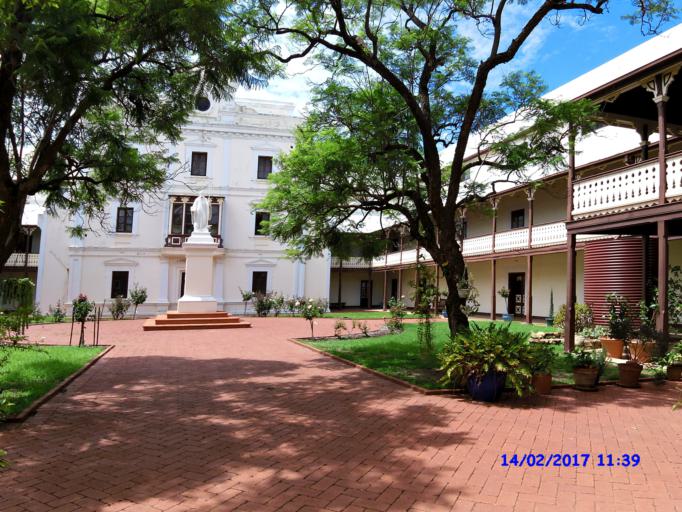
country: AU
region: Western Australia
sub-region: Moora
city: Moora
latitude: -30.9707
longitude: 116.2166
